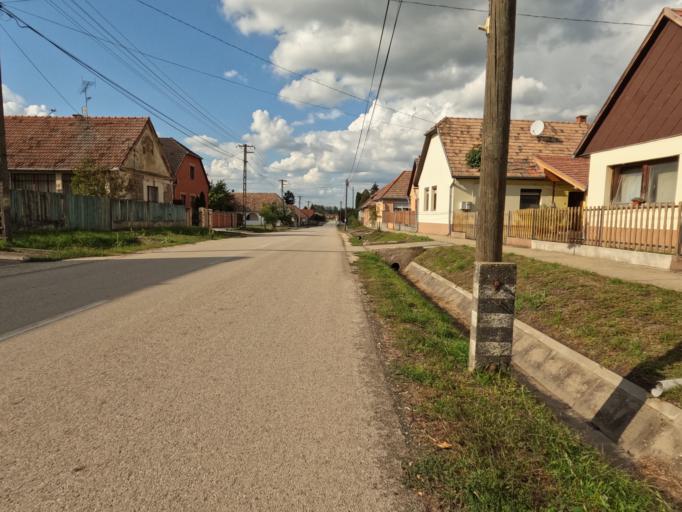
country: HU
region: Tolna
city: Tengelic
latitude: 46.5319
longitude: 18.7102
